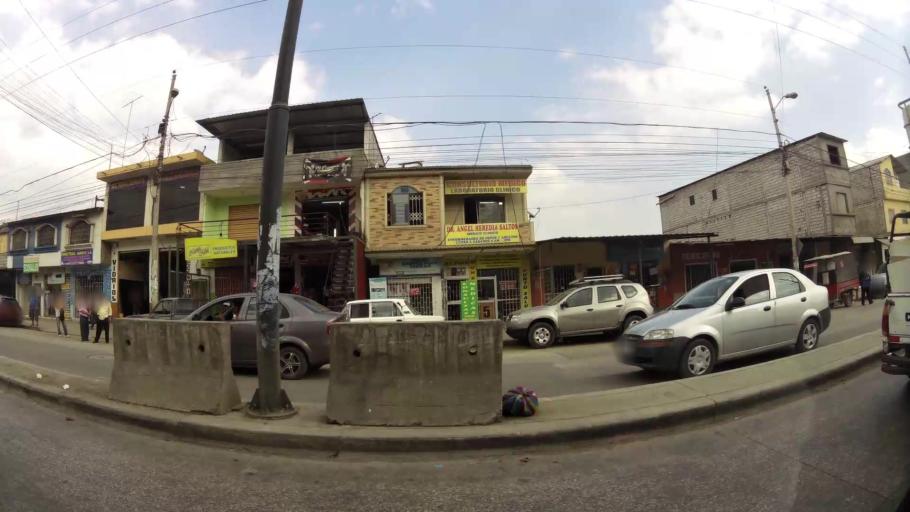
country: EC
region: Guayas
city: Santa Lucia
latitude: -2.1195
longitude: -79.9671
